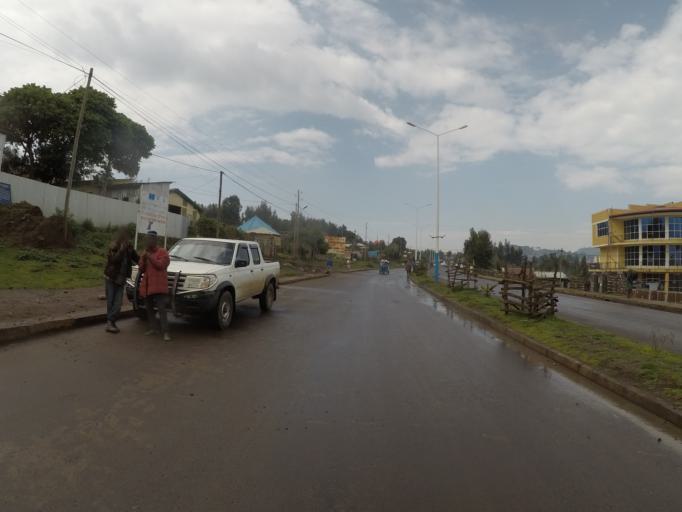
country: ET
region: Amhara
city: Debark'
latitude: 13.1473
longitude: 37.8944
